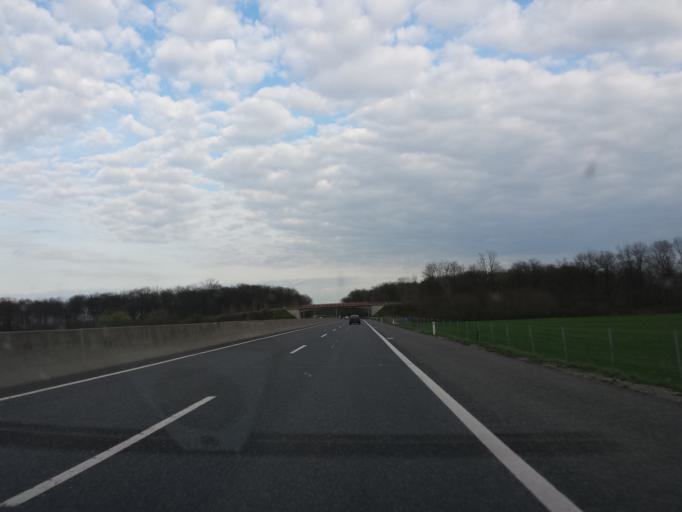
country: AT
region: Lower Austria
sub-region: Politischer Bezirk Korneuburg
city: Stetteldorf am Wagram
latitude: 48.3592
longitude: 15.9916
